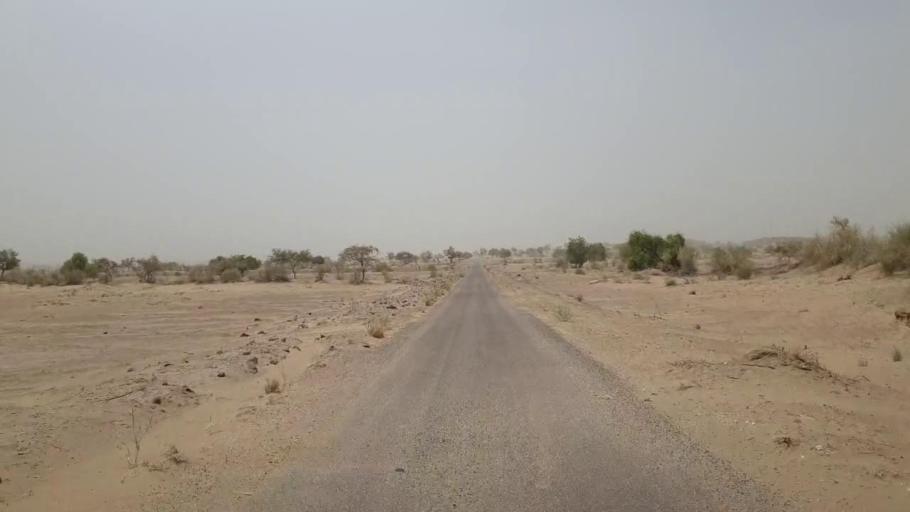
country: PK
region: Sindh
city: Islamkot
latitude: 24.7926
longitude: 70.5129
